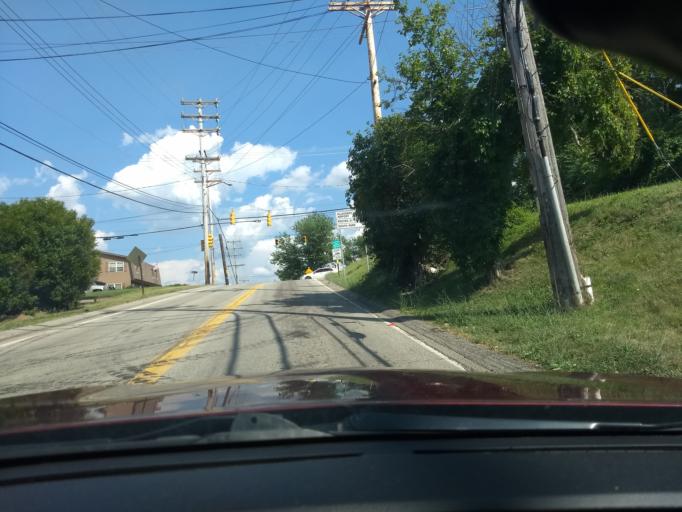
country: US
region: Pennsylvania
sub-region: Allegheny County
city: West Homestead
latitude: 40.3771
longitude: -79.9098
